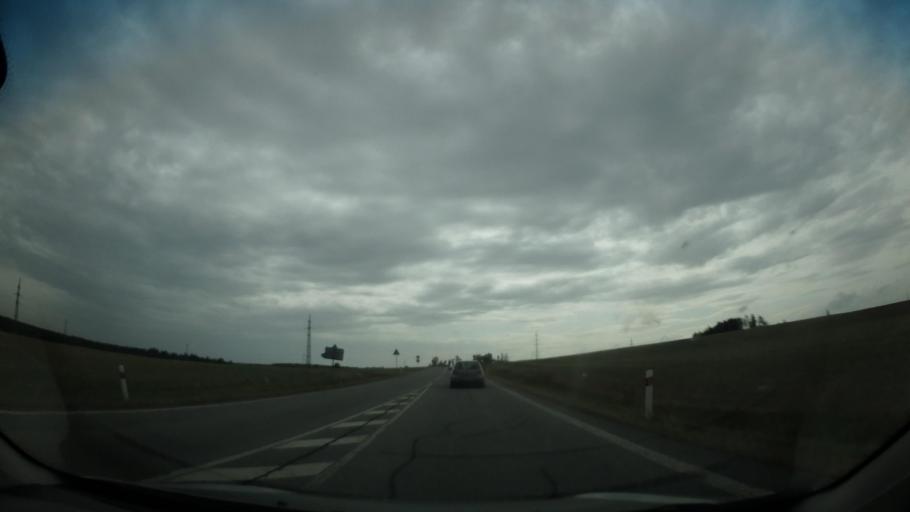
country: CZ
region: Vysocina
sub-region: Okres Zd'ar nad Sazavou
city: Zd'ar nad Sazavou
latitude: 49.5576
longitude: 15.9715
